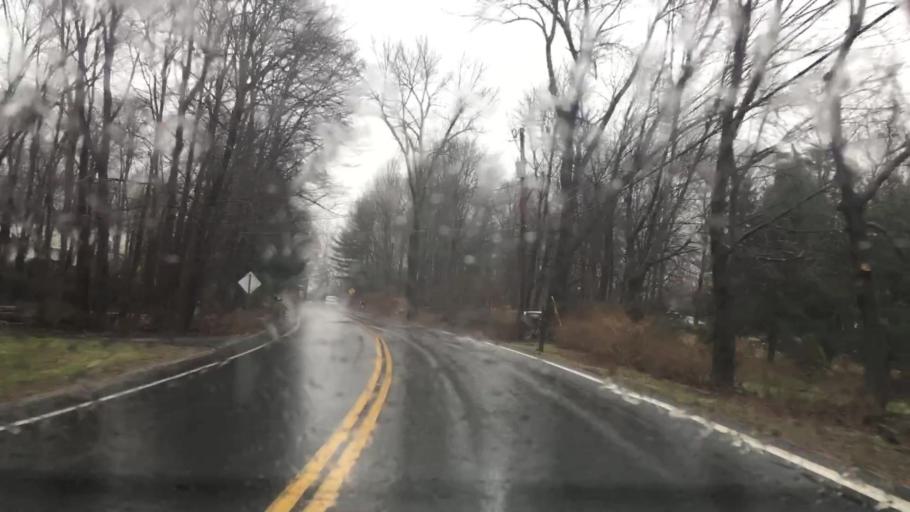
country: US
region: New York
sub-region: Putnam County
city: Putnam Lake
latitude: 41.4603
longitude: -73.5573
